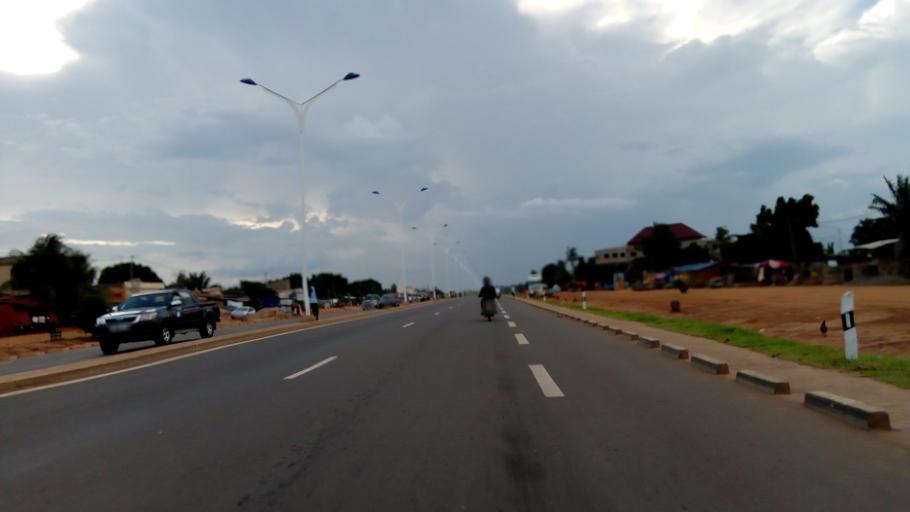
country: TG
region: Maritime
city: Lome
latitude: 6.2415
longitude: 1.2027
